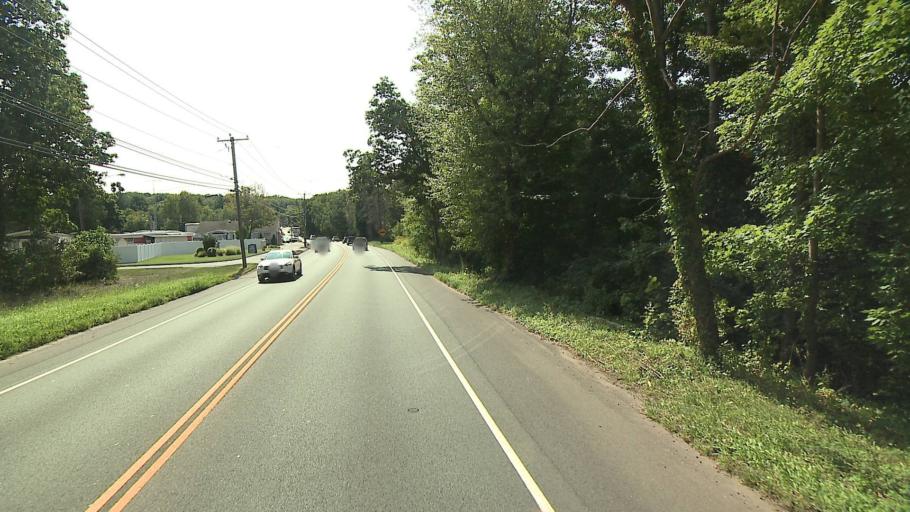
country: US
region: Connecticut
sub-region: Fairfield County
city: Newtown
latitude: 41.3643
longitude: -73.2693
